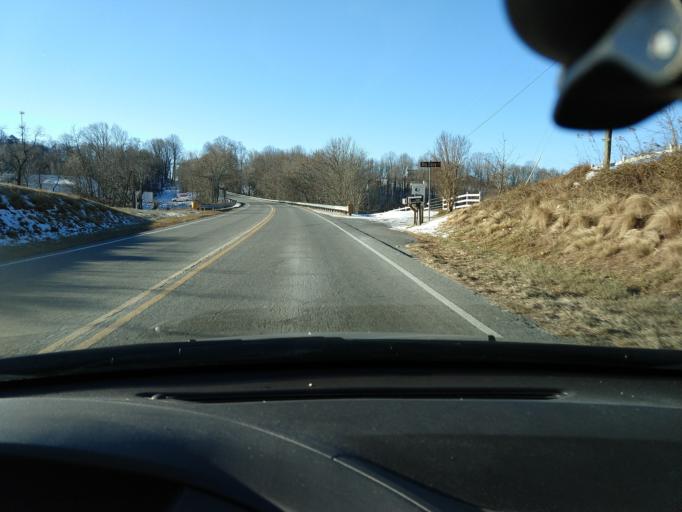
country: US
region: Virginia
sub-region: City of Bedford
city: Bedford
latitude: 37.2844
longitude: -79.5520
